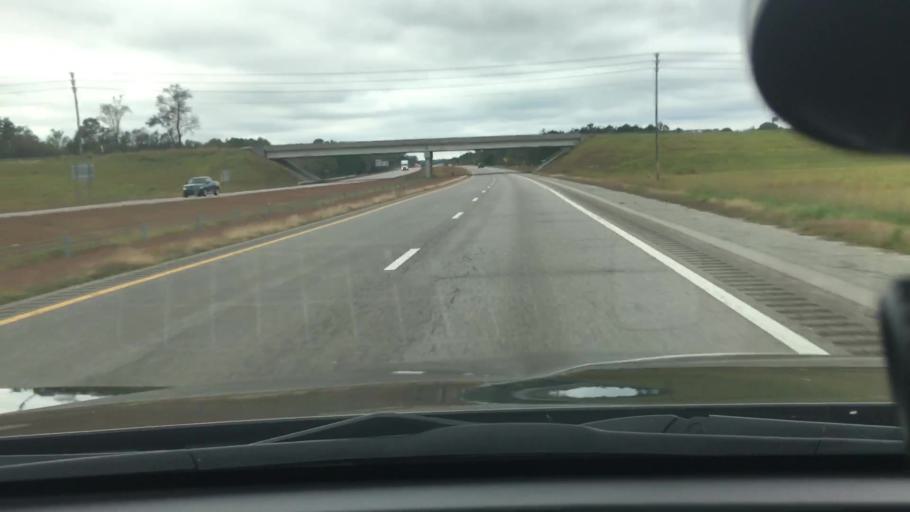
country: US
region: North Carolina
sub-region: Wilson County
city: Wilson
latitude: 35.6740
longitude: -77.9050
